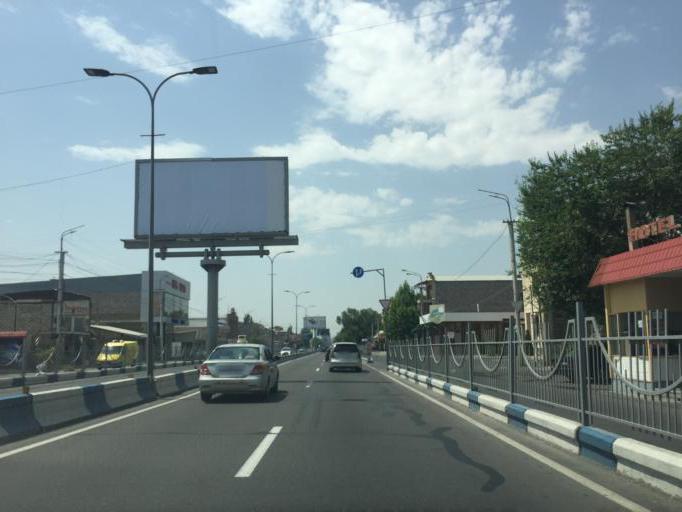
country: AM
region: Ararat
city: Argavand
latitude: 40.1589
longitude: 44.4298
